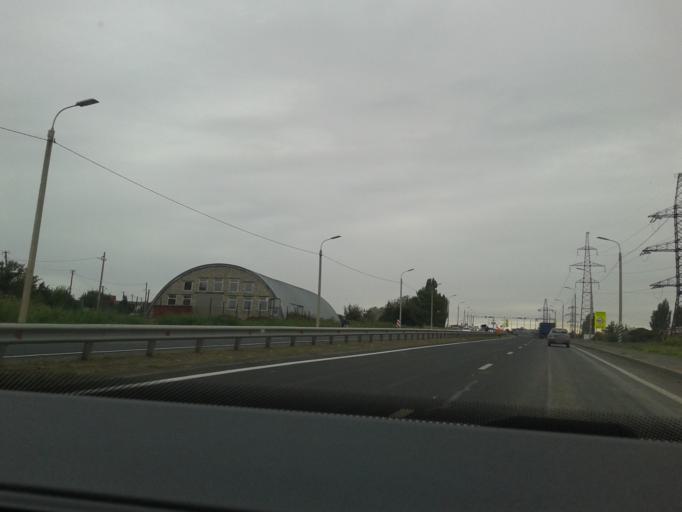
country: RU
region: Volgograd
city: Gorodishche
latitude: 48.7840
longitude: 44.4625
